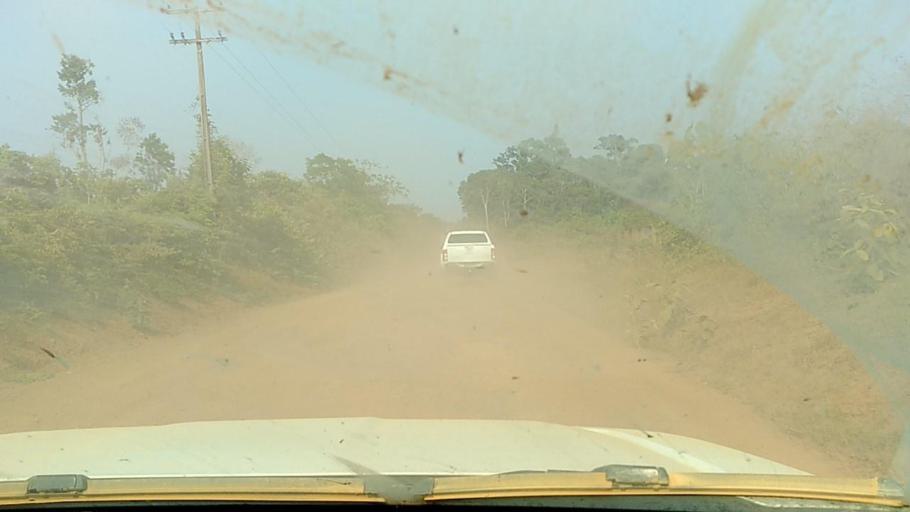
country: BR
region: Rondonia
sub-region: Porto Velho
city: Porto Velho
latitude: -8.8405
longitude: -64.1539
